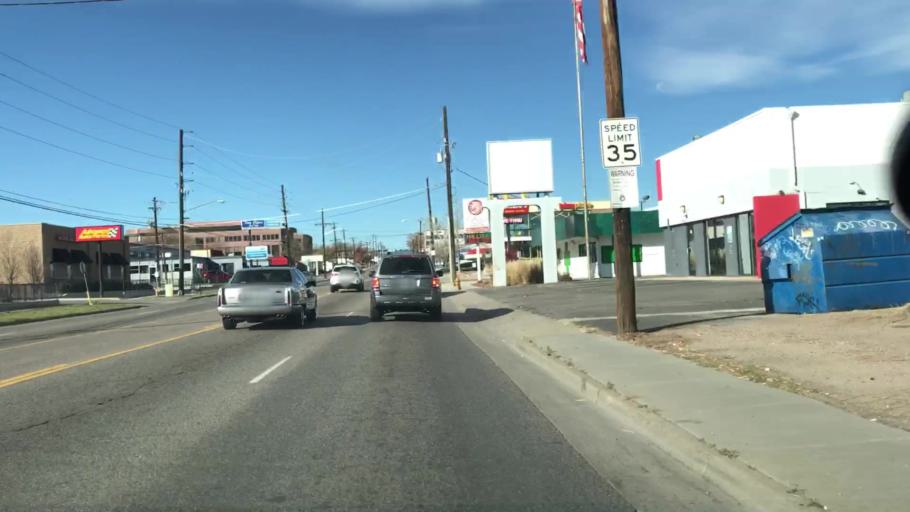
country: US
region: Colorado
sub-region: Arapahoe County
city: Glendale
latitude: 39.6785
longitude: -104.9140
